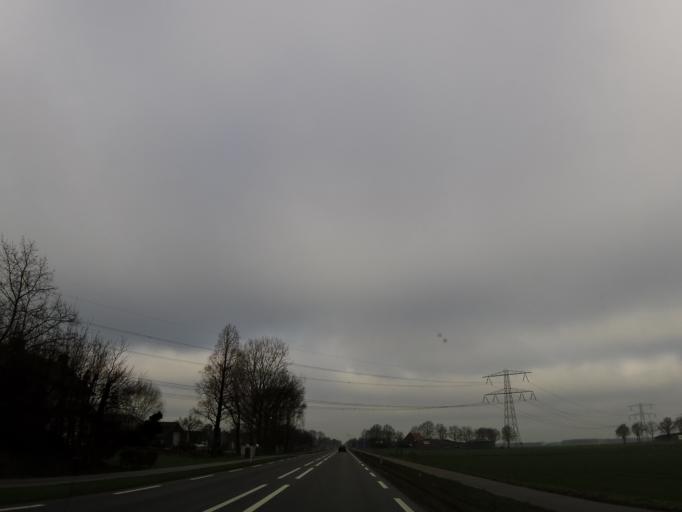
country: NL
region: Limburg
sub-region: Gemeente Venray
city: Venray
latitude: 51.4701
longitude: 5.9329
